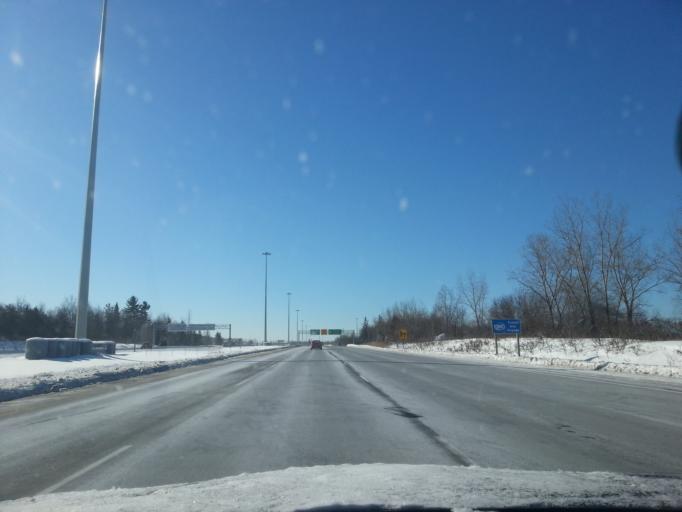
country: CA
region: Ontario
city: Bells Corners
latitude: 45.2794
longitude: -75.9600
